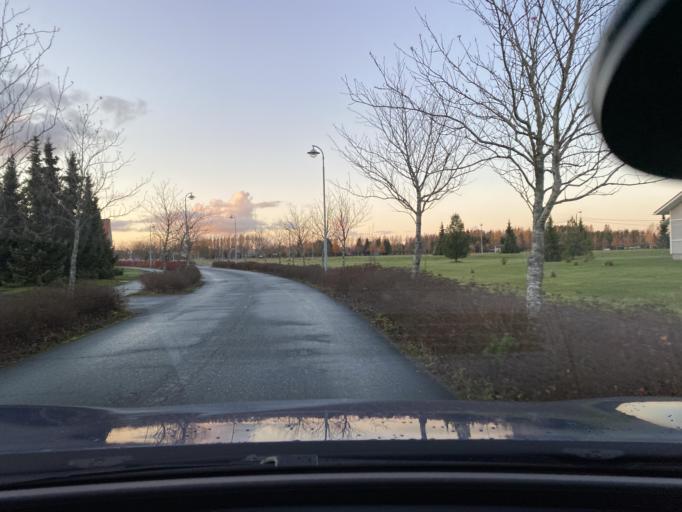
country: FI
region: Satakunta
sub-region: Pori
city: Huittinen
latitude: 61.1822
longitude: 22.7037
